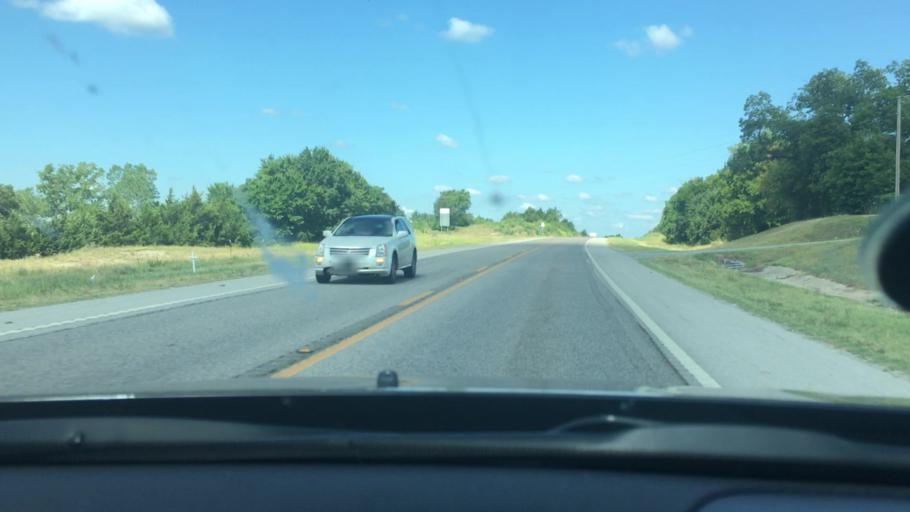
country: US
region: Oklahoma
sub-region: Carter County
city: Dickson
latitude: 34.1004
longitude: -96.9625
